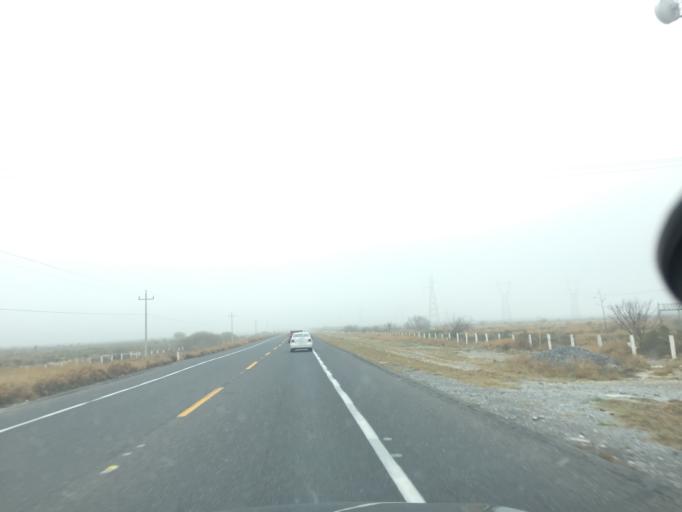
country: MX
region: Coahuila
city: Castanos
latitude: 26.5110
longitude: -101.1269
